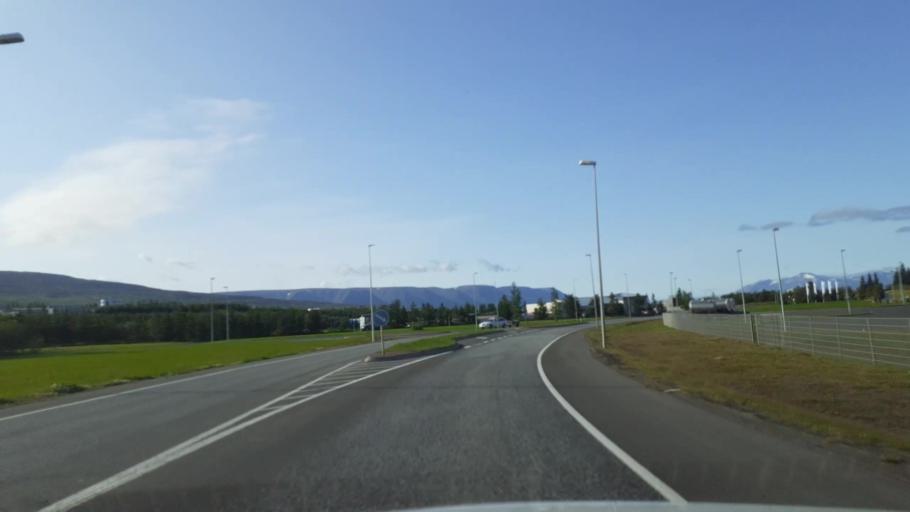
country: IS
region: Northeast
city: Akureyri
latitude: 65.6747
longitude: -18.1284
